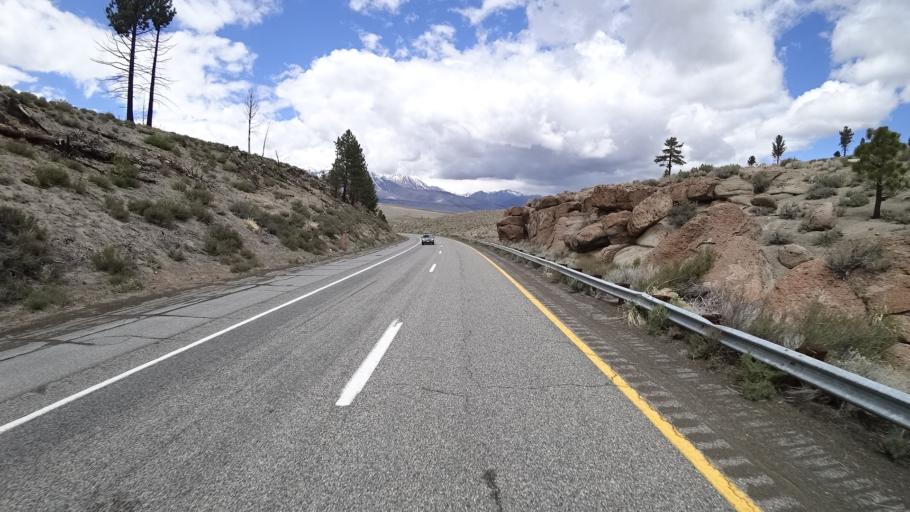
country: US
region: California
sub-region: Mono County
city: Mammoth Lakes
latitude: 37.8282
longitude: -119.0663
